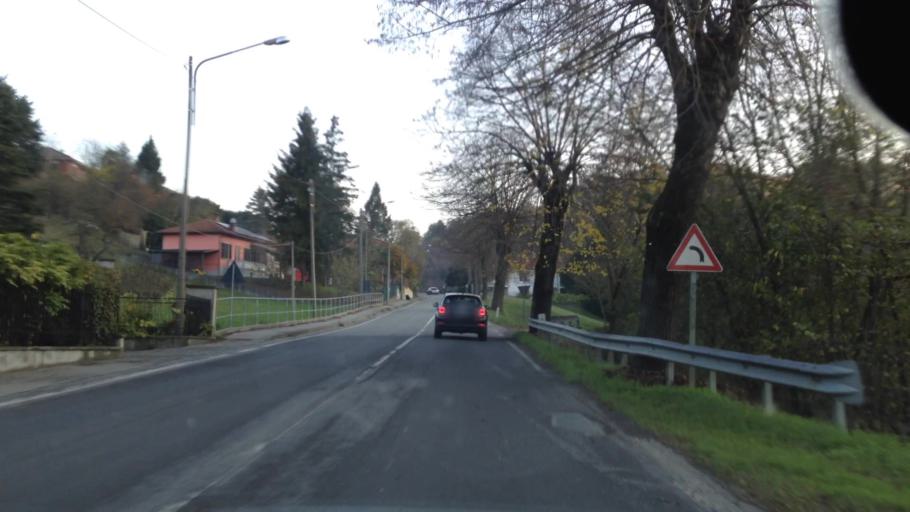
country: IT
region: Piedmont
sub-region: Provincia di Torino
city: Brozolo
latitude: 45.1213
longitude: 8.0595
